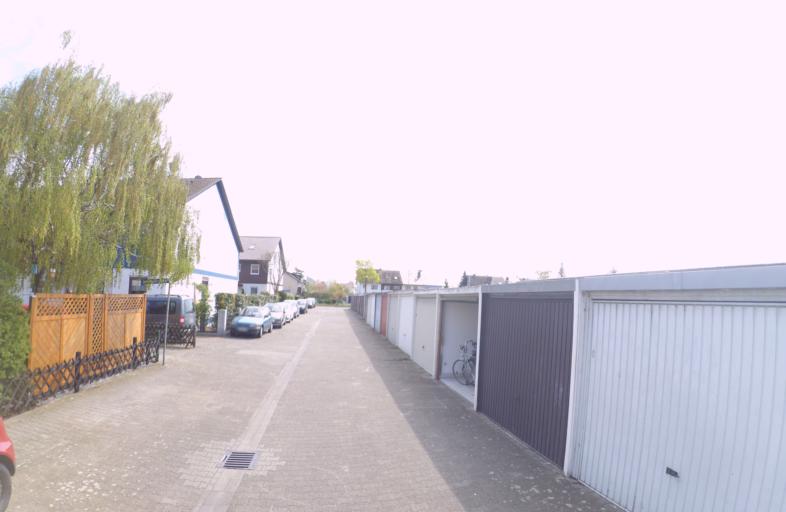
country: DE
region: Baden-Wuerttemberg
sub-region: Karlsruhe Region
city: Ladenburg
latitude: 49.4701
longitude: 8.5897
